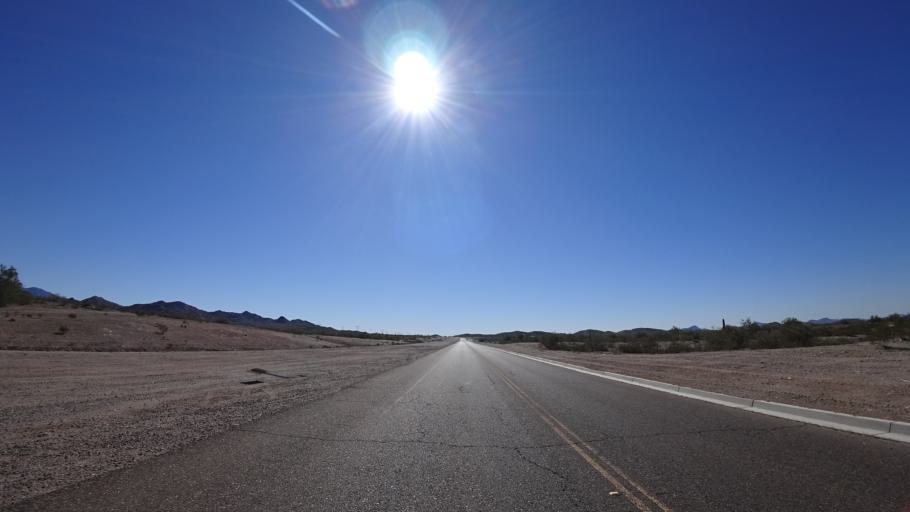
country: US
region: Arizona
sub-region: Maricopa County
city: Goodyear
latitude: 33.3753
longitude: -112.4204
